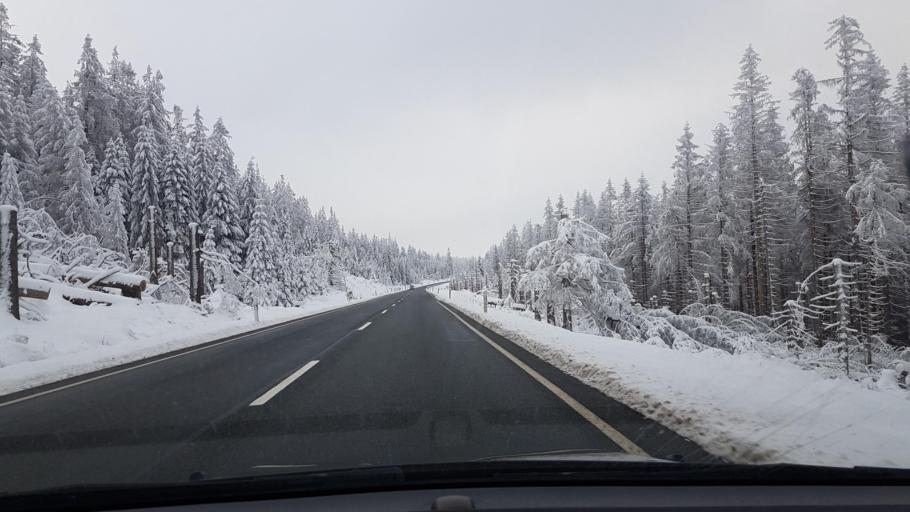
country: DE
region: Lower Saxony
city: Altenau
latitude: 51.7675
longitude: 10.4779
